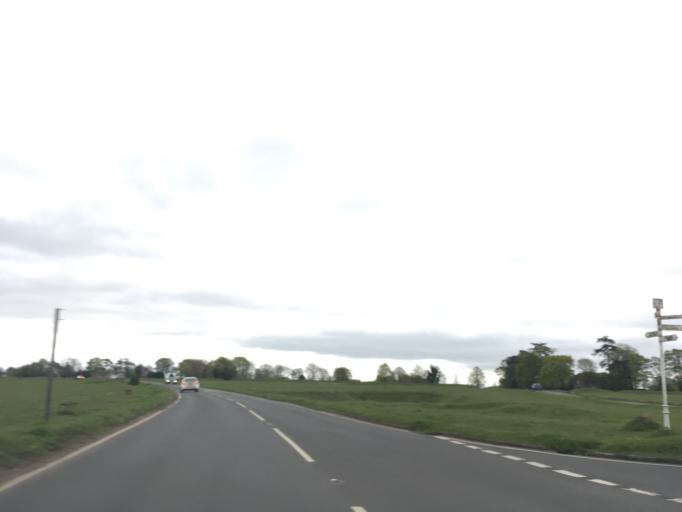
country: GB
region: England
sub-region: Gloucestershire
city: Minchinhampton
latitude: 51.7104
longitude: -2.2057
